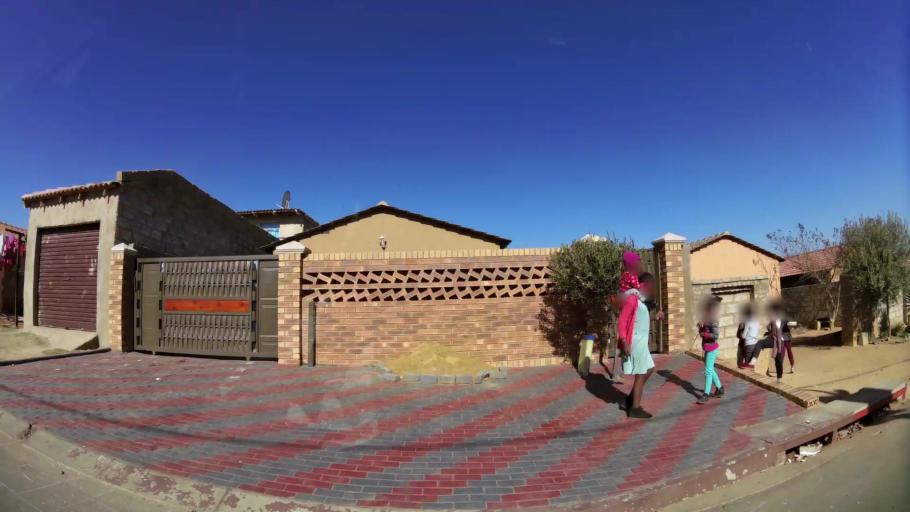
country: ZA
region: Gauteng
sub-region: Ekurhuleni Metropolitan Municipality
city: Tembisa
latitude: -26.0313
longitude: 28.2225
